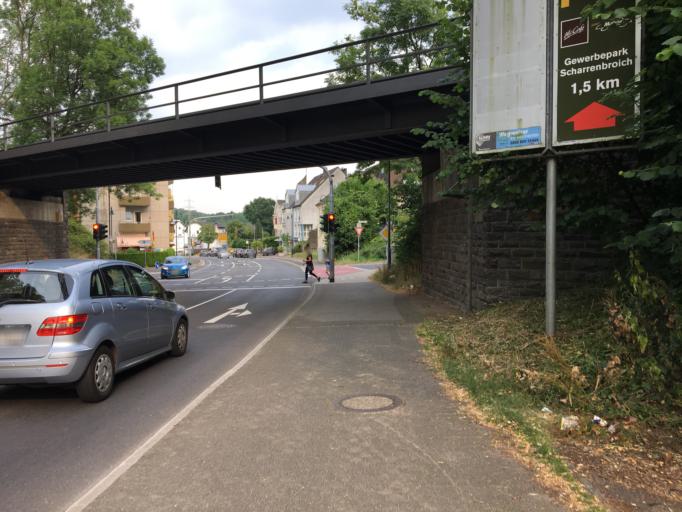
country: DE
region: North Rhine-Westphalia
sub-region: Regierungsbezirk Koln
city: Rosrath
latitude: 50.8950
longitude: 7.1773
